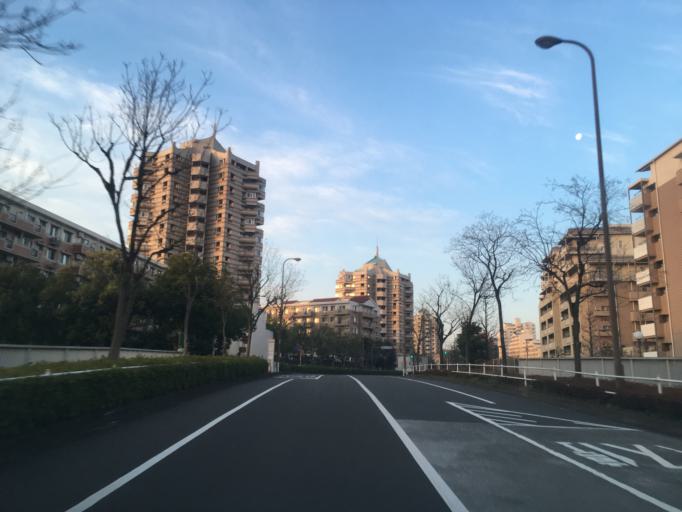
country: JP
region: Tokyo
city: Hachioji
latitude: 35.6142
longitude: 139.3717
